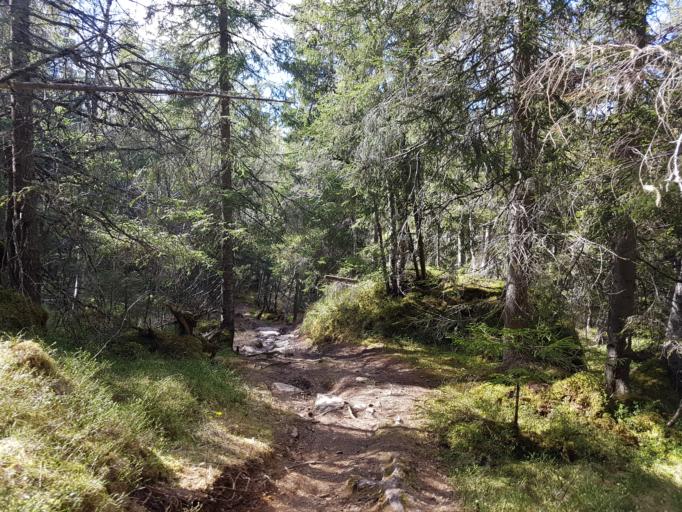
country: NO
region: Sor-Trondelag
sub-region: Trondheim
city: Trondheim
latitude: 63.4448
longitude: 10.3036
